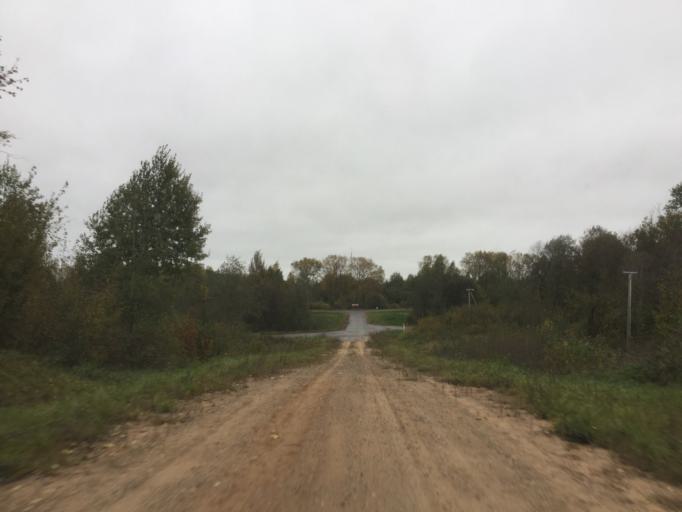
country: BY
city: Novolukoml'
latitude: 54.7334
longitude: 29.1401
